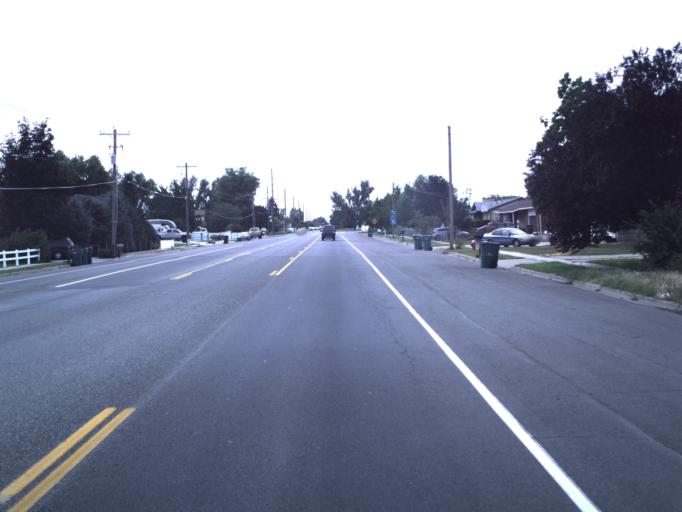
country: US
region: Utah
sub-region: Weber County
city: West Haven
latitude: 41.1713
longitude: -112.0645
